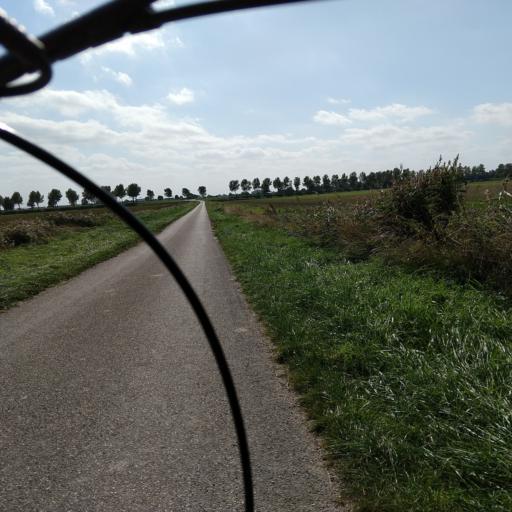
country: NL
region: Zeeland
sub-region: Gemeente Goes
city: Goes
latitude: 51.5626
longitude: 3.8229
